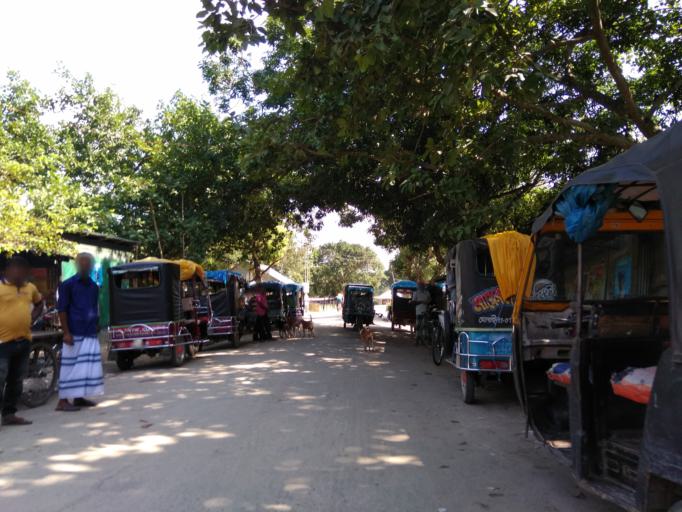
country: IN
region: West Bengal
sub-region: Koch Bihar
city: Haldibari
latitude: 26.2243
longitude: 88.6780
